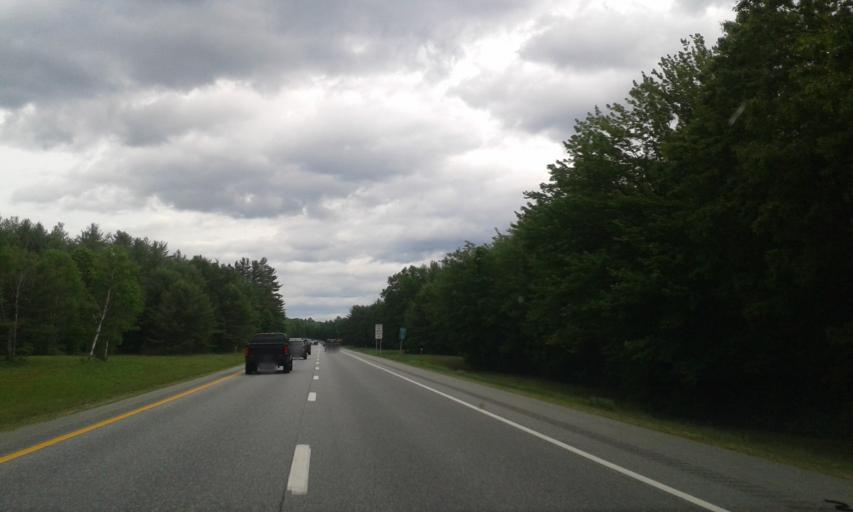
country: US
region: New Hampshire
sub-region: Merrimack County
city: East Concord
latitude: 43.2825
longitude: -71.5675
